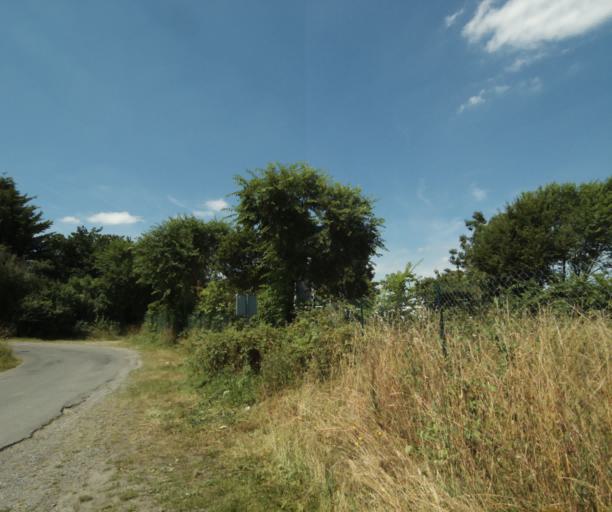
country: FR
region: Pays de la Loire
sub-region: Departement de la Mayenne
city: Laval
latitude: 48.0813
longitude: -0.7385
